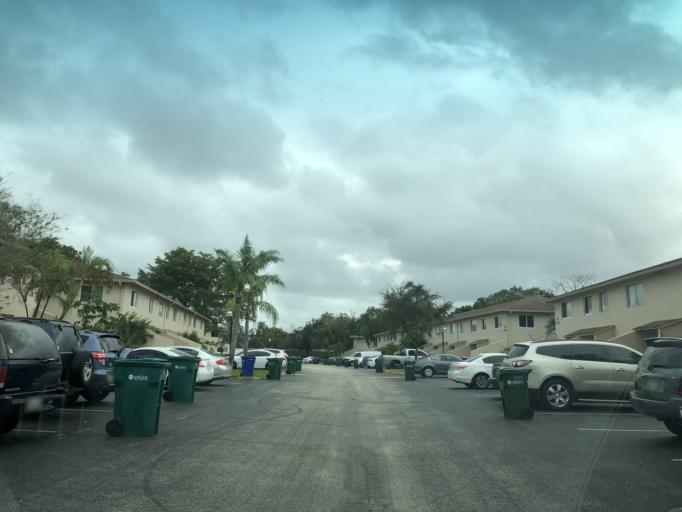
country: US
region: Florida
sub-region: Broward County
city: Margate
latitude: 26.2498
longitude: -80.2326
